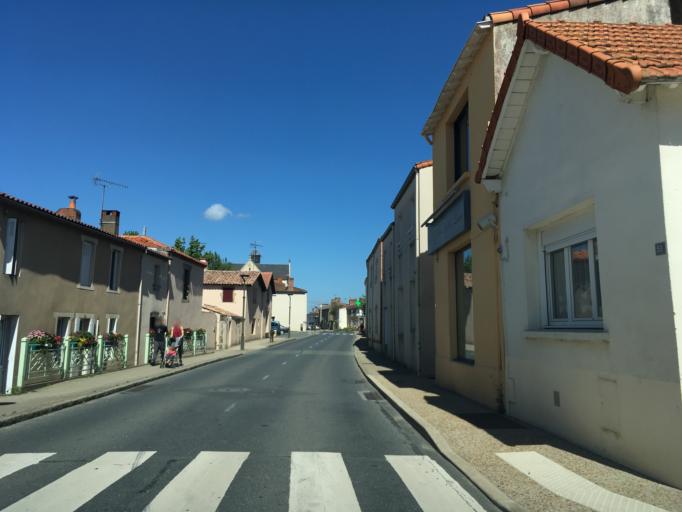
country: FR
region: Pays de la Loire
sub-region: Departement de la Vendee
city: Saint-Georges-de-Montaigu
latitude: 46.9464
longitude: -1.2933
